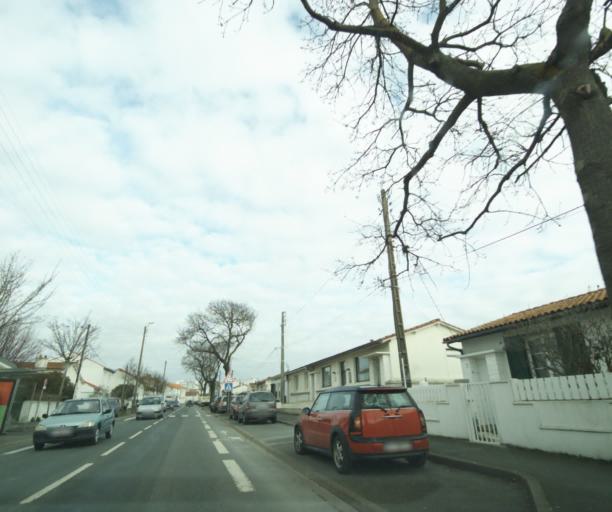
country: FR
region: Poitou-Charentes
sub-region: Departement de la Charente-Maritime
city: La Rochelle
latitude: 46.1654
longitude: -1.1900
